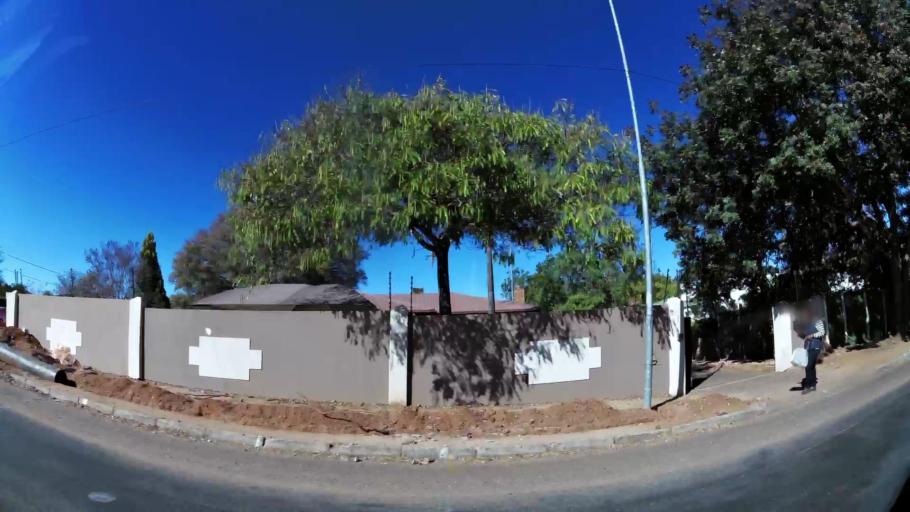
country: ZA
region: Limpopo
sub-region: Capricorn District Municipality
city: Polokwane
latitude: -23.9081
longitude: 29.4698
